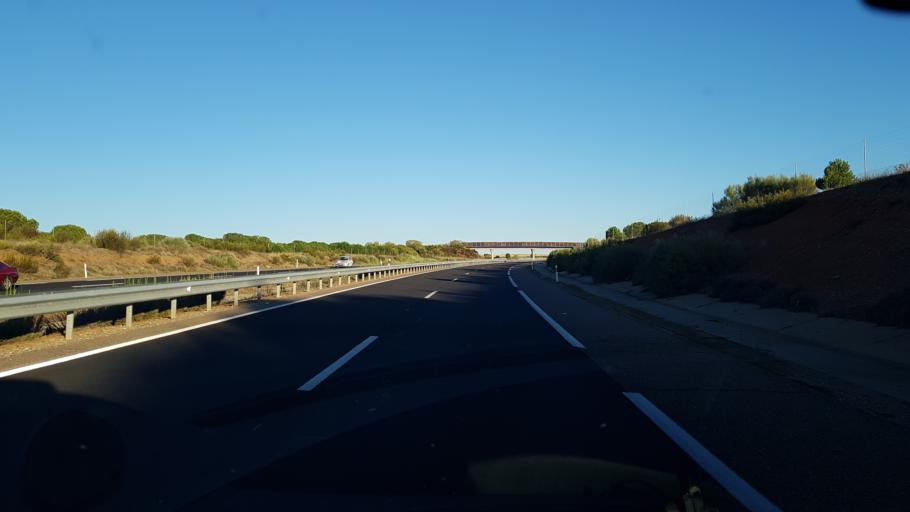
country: ES
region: Castille and Leon
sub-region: Provincia de Zamora
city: Pozoantiguo
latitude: 41.5498
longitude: -5.4570
